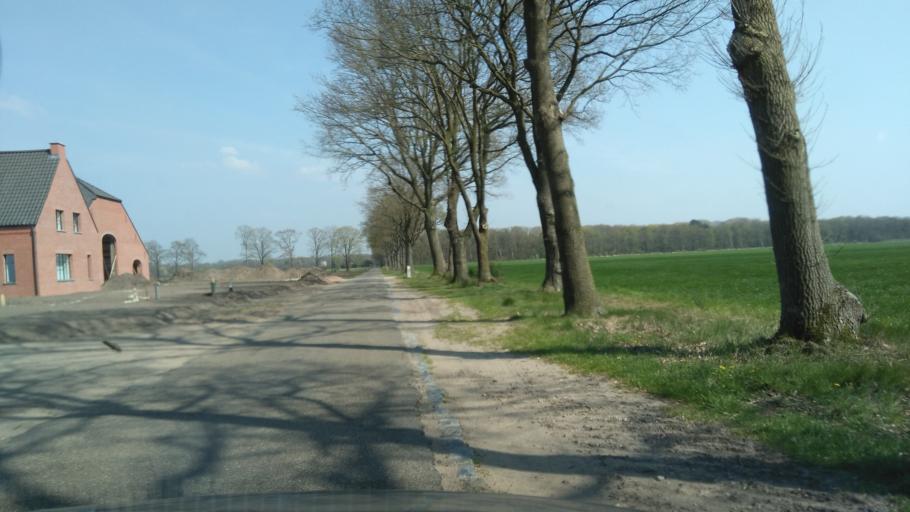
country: BE
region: Flanders
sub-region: Provincie Antwerpen
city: Baarle-Hertog
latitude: 51.4048
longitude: 4.9158
